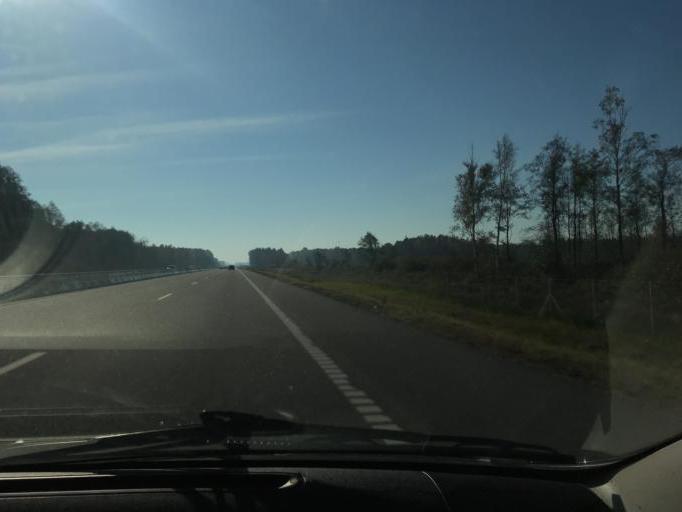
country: BY
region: Minsk
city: Slutsk
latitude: 53.2526
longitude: 27.5501
